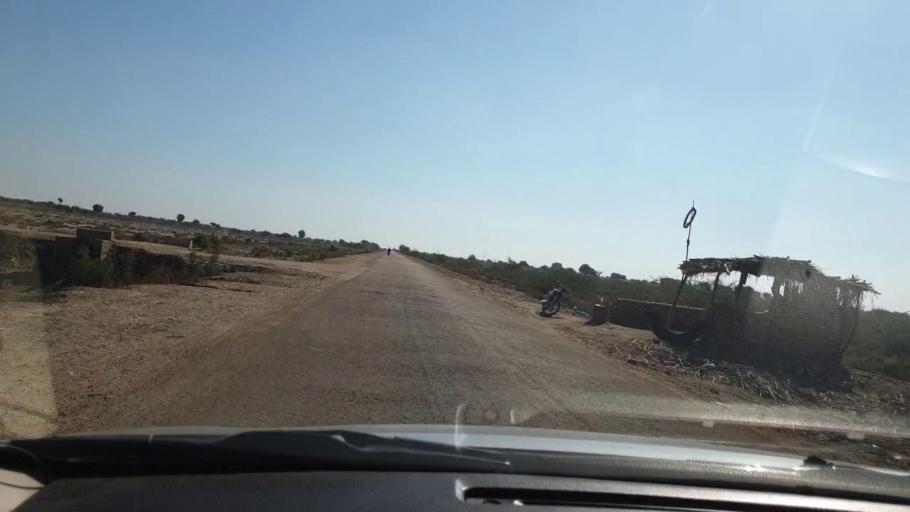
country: PK
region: Sindh
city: Berani
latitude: 25.7737
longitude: 68.9541
